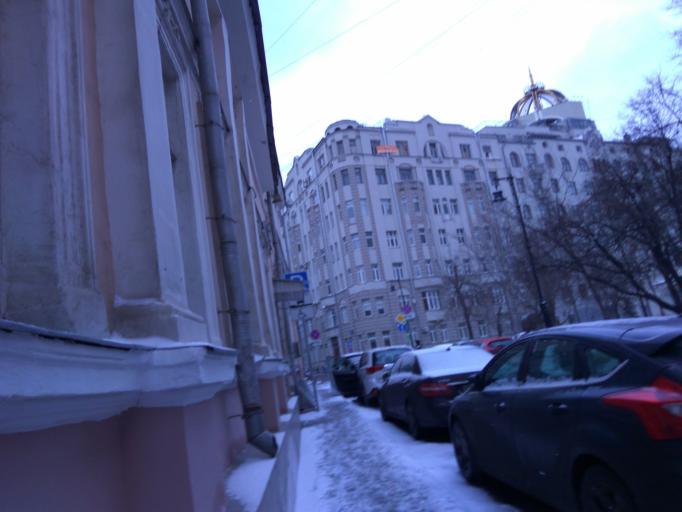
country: RU
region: Moscow
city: Moscow
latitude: 55.7538
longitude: 37.5912
